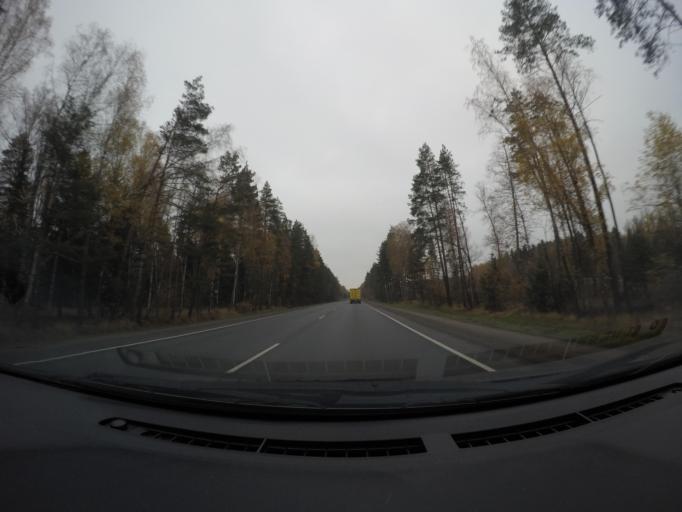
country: RU
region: Moskovskaya
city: Gzhel'
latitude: 55.5632
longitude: 38.3953
